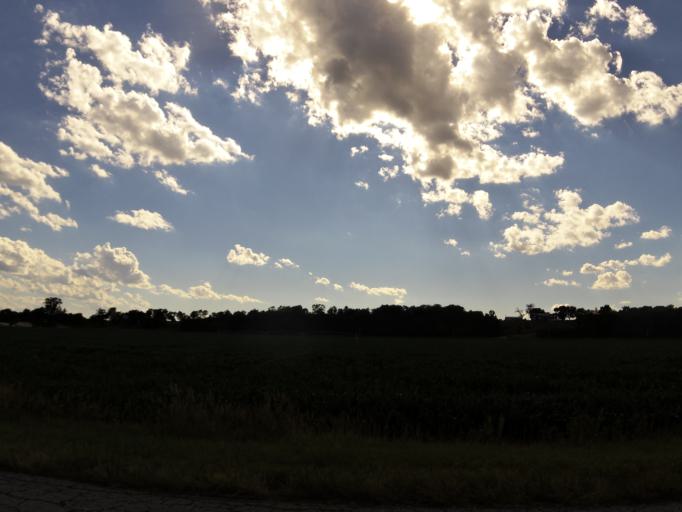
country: US
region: Illinois
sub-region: Adams County
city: Quincy
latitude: 39.9536
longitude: -91.5187
